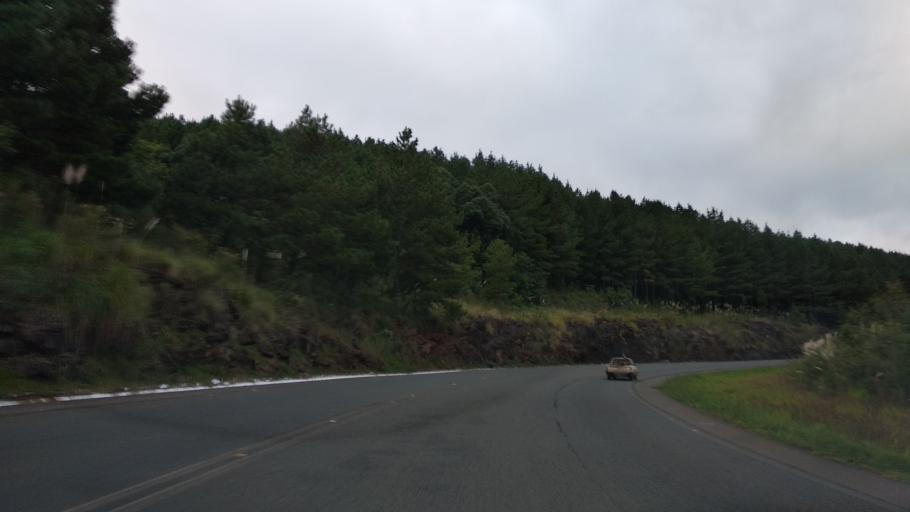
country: BR
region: Santa Catarina
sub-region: Campos Novos
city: Campos Novos
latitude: -27.4896
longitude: -50.9724
